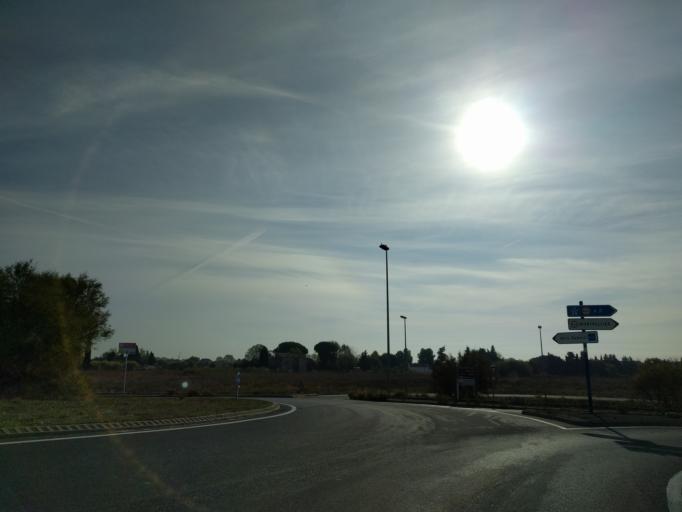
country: FR
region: Languedoc-Roussillon
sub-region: Departement de l'Herault
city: Lattes
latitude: 43.5809
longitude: 3.8993
